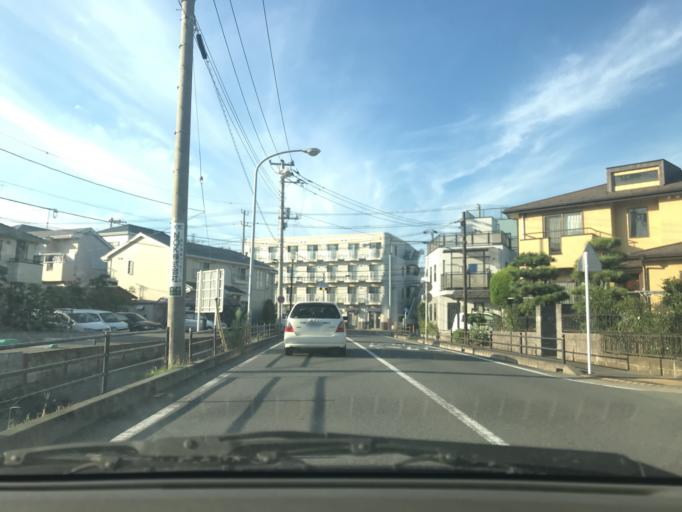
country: JP
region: Kanagawa
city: Fujisawa
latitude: 35.3464
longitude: 139.4617
